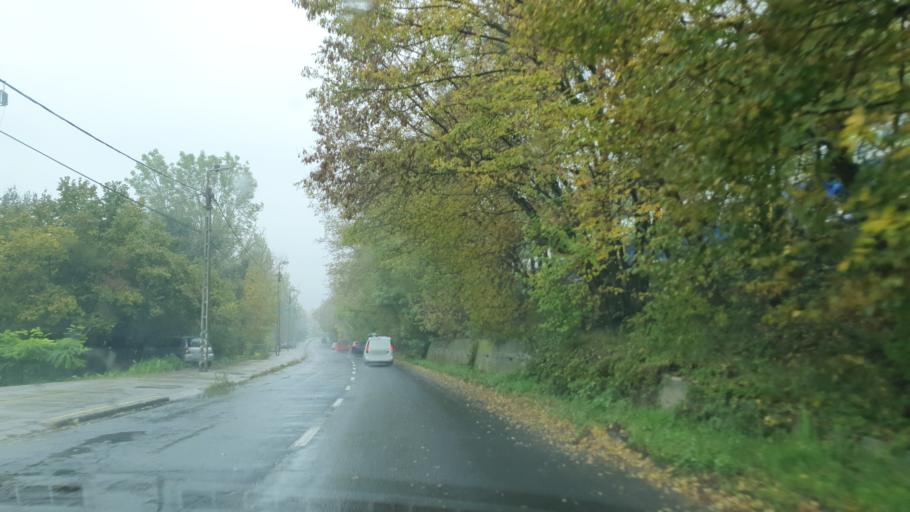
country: HU
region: Komarom-Esztergom
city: Pilismarot
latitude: 47.7864
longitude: 18.9107
